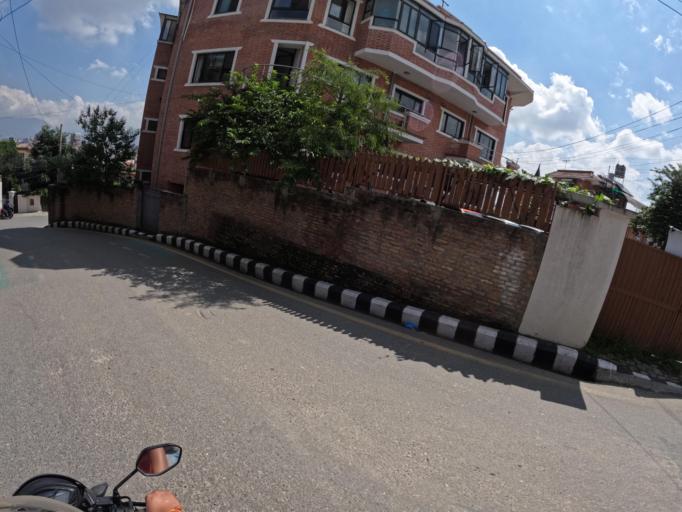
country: NP
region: Central Region
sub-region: Bagmati Zone
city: Patan
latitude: 27.6856
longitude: 85.3128
